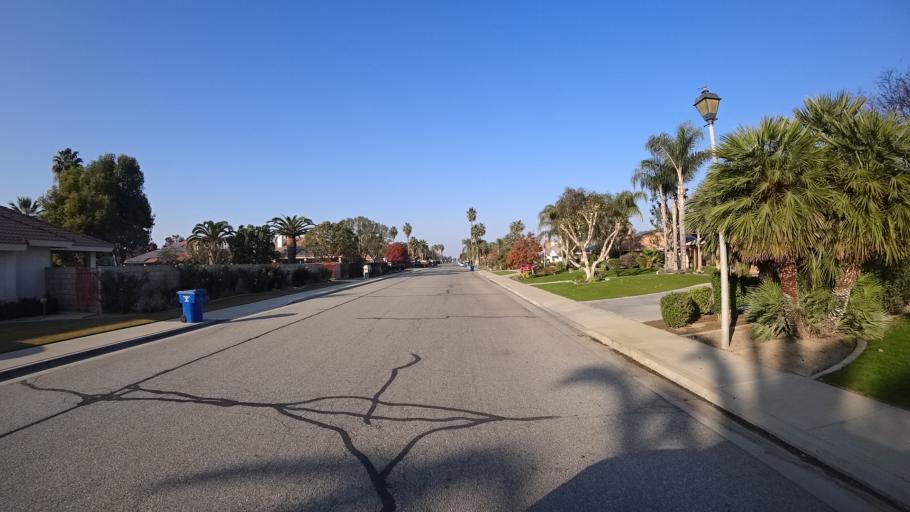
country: US
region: California
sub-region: Kern County
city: Rosedale
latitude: 35.3880
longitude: -119.1500
